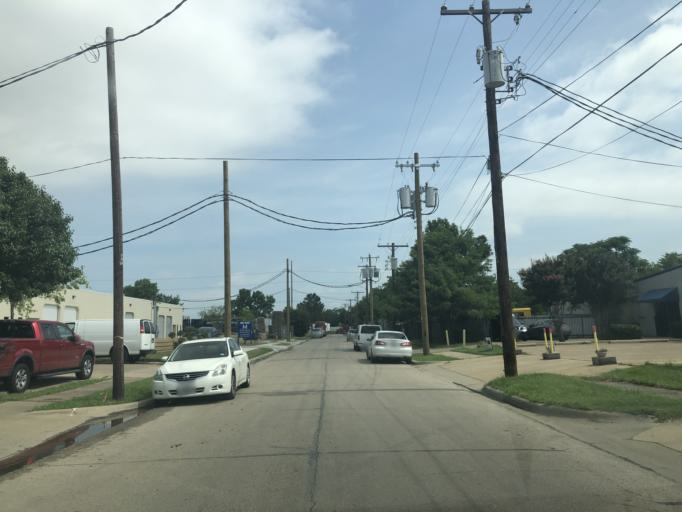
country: US
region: Texas
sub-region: Dallas County
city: Cockrell Hill
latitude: 32.8048
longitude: -96.8784
